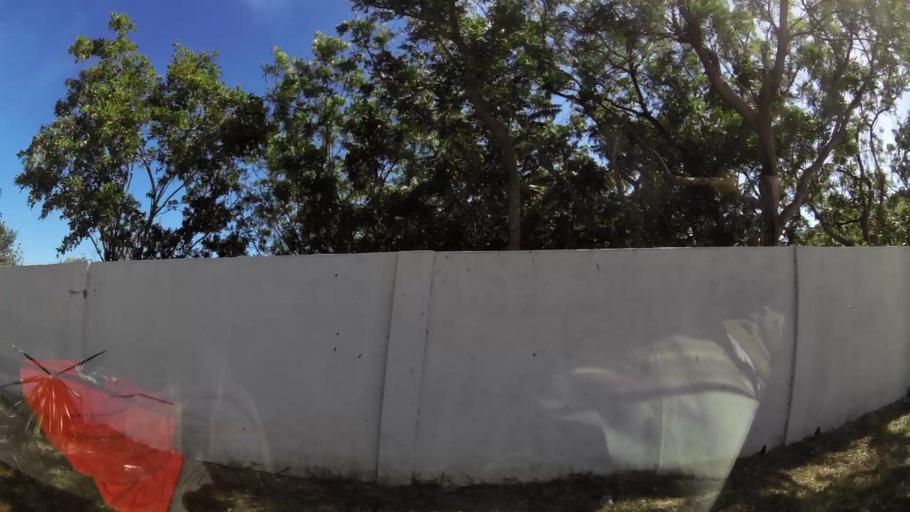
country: AG
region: Saint Paul
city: Falmouth
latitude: 17.0260
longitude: -61.7400
